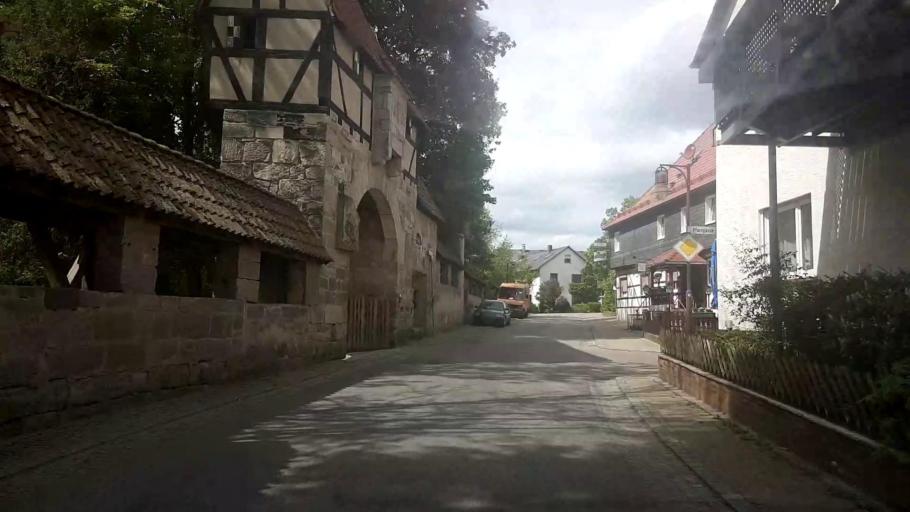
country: DE
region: Bavaria
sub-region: Upper Franconia
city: Untersiemau
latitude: 50.1930
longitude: 10.9748
